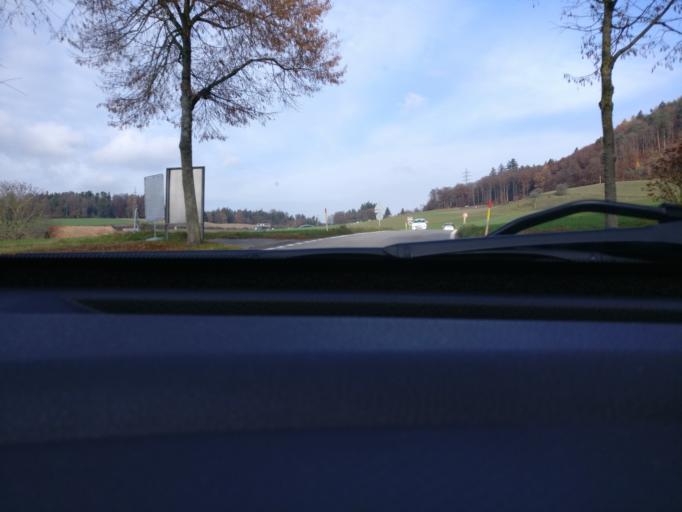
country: CH
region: Bern
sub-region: Bern-Mittelland District
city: Bolligen
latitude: 46.9862
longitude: 7.4801
